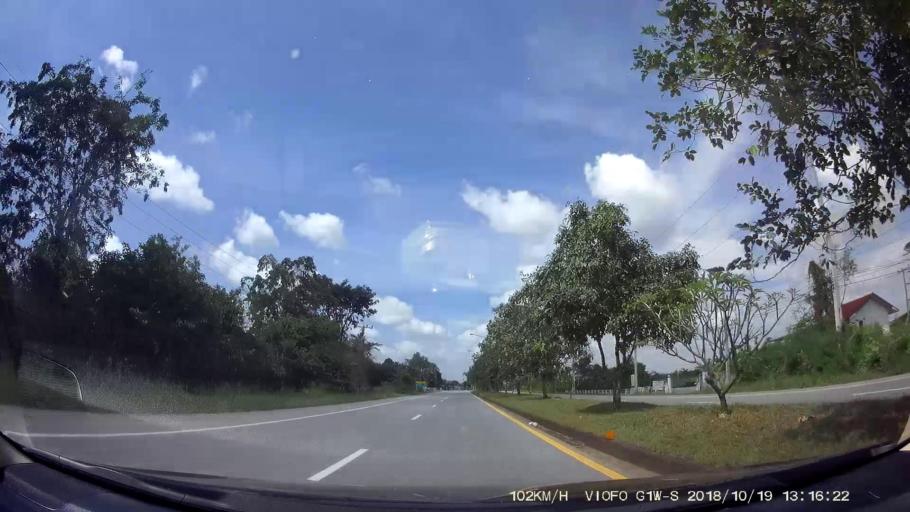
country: TH
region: Chaiyaphum
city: Chatturat
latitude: 15.4028
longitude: 101.8365
